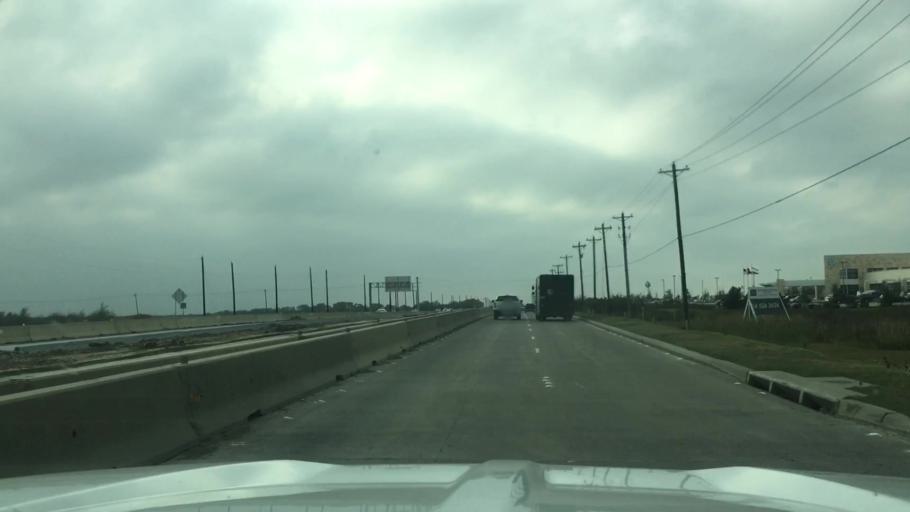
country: US
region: Texas
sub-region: Collin County
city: Prosper
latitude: 33.2194
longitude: -96.8285
